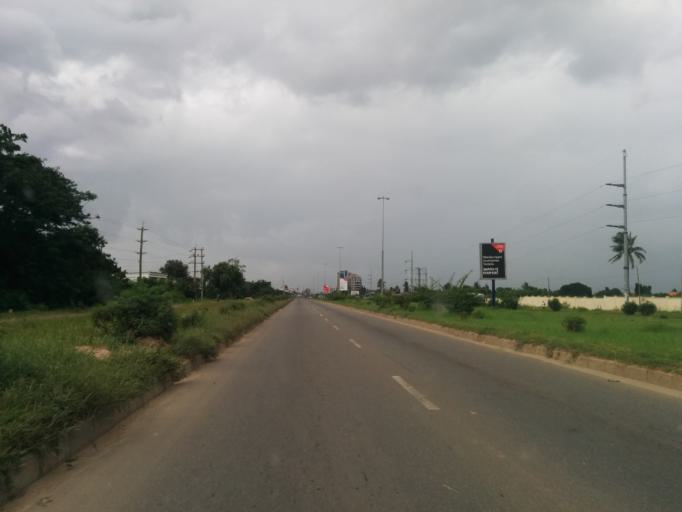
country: TZ
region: Dar es Salaam
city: Magomeni
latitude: -6.7810
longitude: 39.2156
